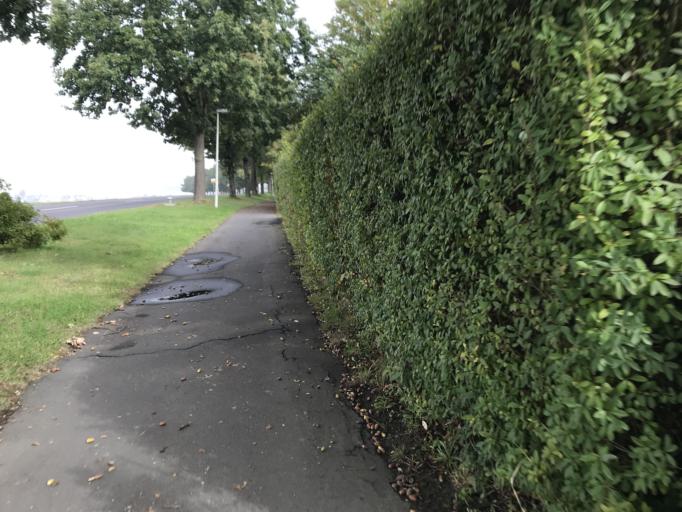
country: DE
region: Hesse
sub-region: Regierungsbezirk Kassel
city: Baunatal
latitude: 51.2043
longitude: 9.4296
